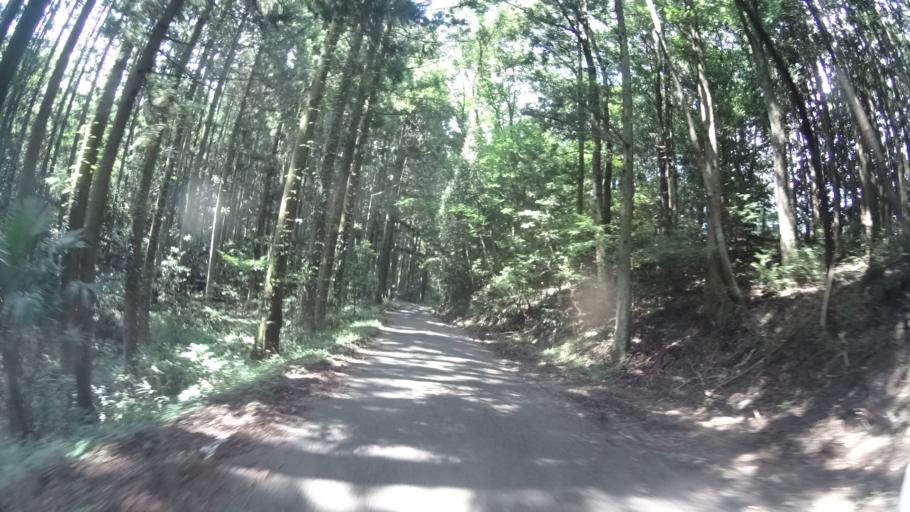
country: JP
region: Yamaguchi
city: Hagi
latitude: 34.4973
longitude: 131.5589
